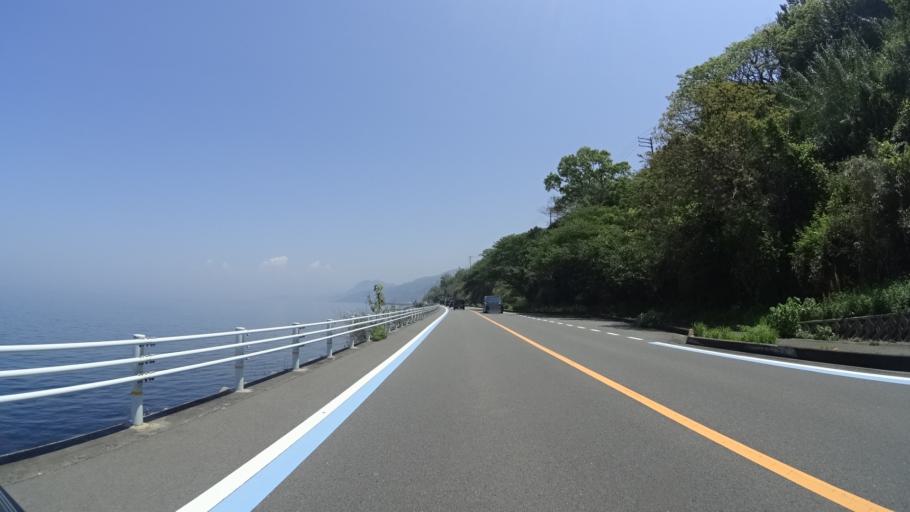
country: JP
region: Ehime
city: Ozu
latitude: 33.6452
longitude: 132.5571
